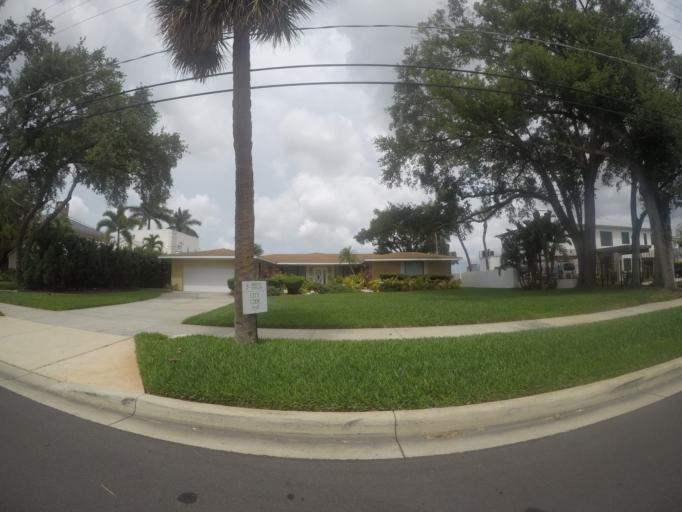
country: US
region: Florida
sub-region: Hillsborough County
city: Tampa
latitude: 27.9348
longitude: -82.4601
